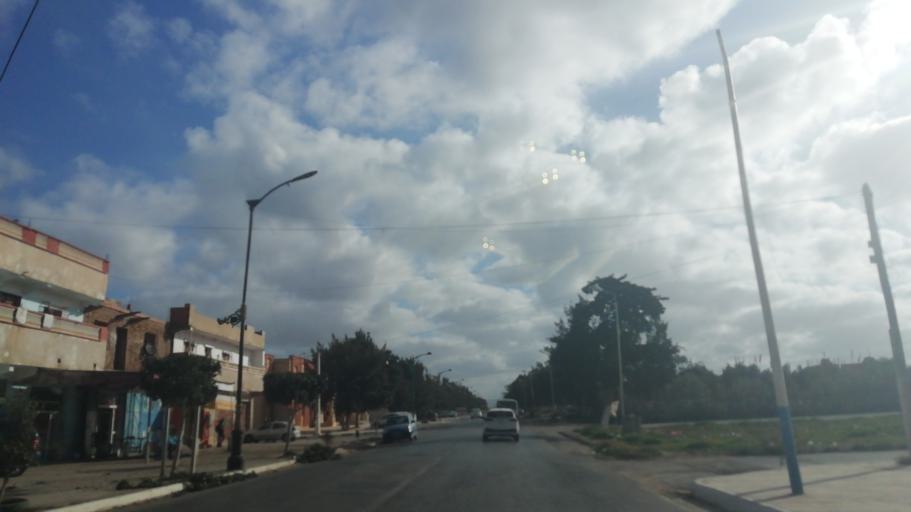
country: DZ
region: Relizane
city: Mazouna
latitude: 36.2548
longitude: 0.5784
